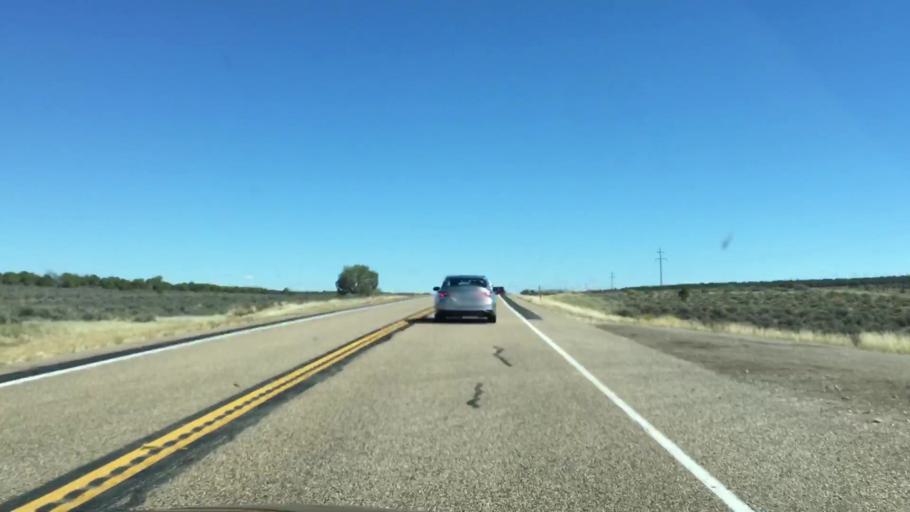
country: US
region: Utah
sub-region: Kane County
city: Kanab
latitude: 37.1349
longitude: -112.0848
